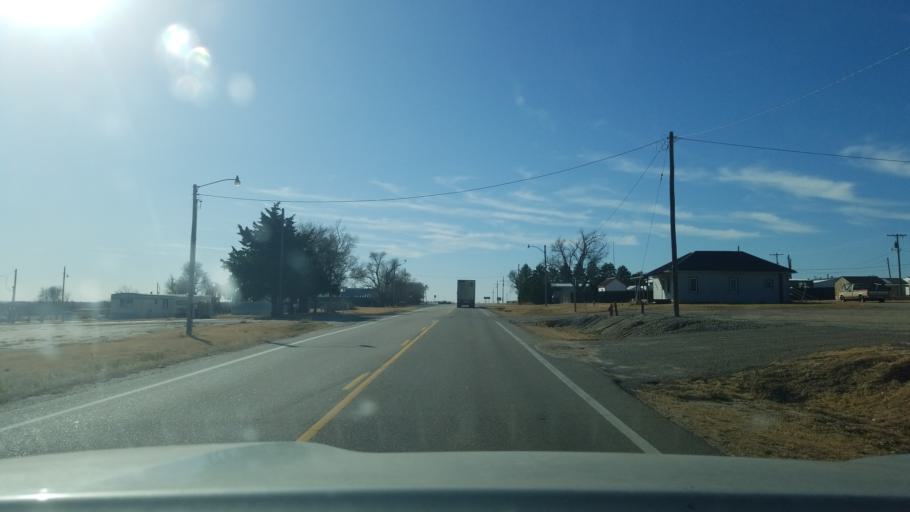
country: US
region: Kansas
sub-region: Ness County
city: Ness City
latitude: 38.4445
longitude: -99.9049
